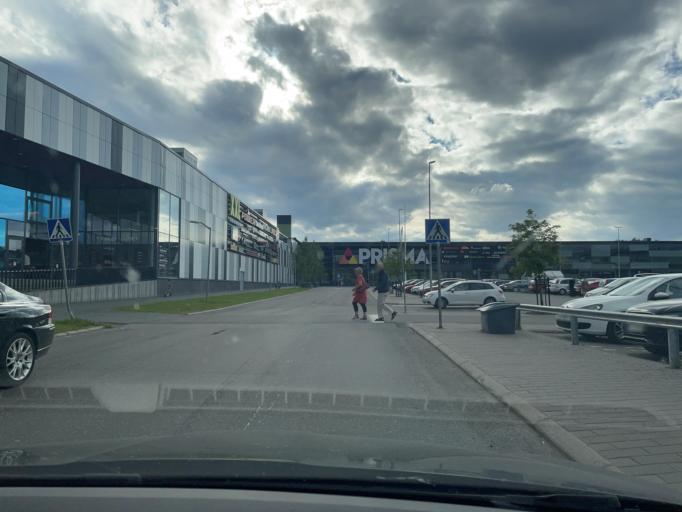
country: FI
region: Central Finland
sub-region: Jyvaeskylae
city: Jyvaeskylae
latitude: 62.2567
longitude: 25.7766
